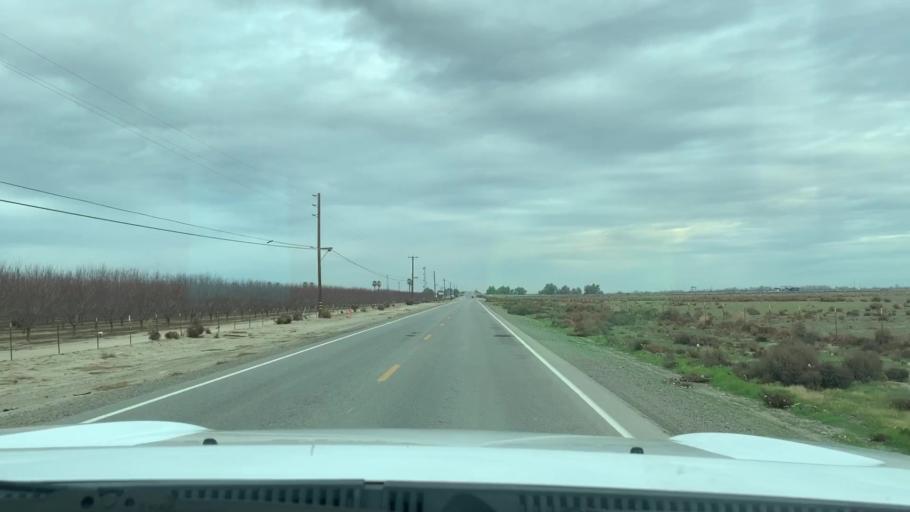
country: US
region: California
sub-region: Kern County
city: Rosedale
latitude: 35.2832
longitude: -119.2526
